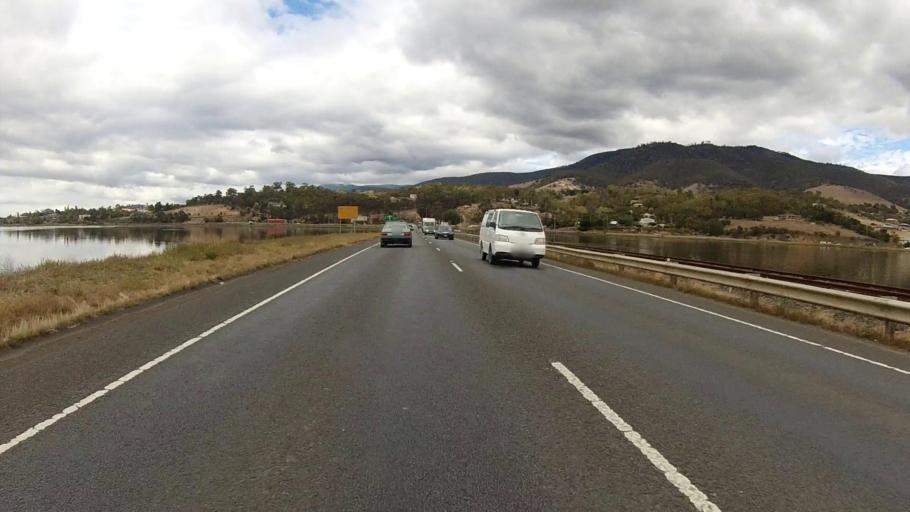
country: AU
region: Tasmania
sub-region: Glenorchy
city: Granton
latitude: -42.7455
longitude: 147.2249
